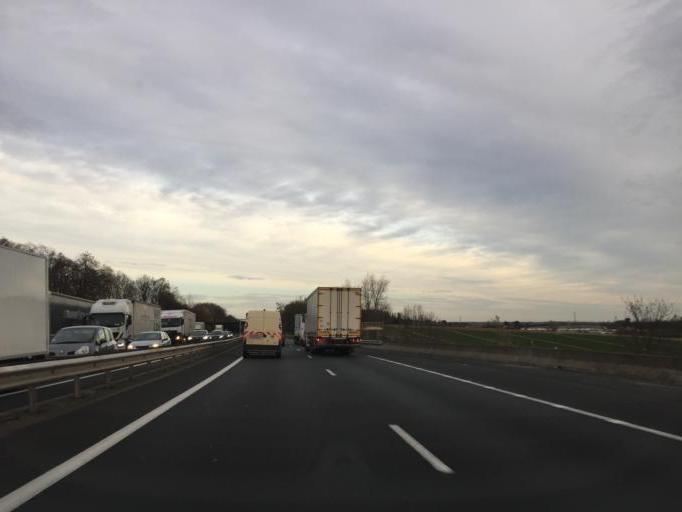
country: FR
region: Rhone-Alpes
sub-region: Departement du Rhone
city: Rillieux-la-Pape
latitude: 45.8398
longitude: 4.9165
